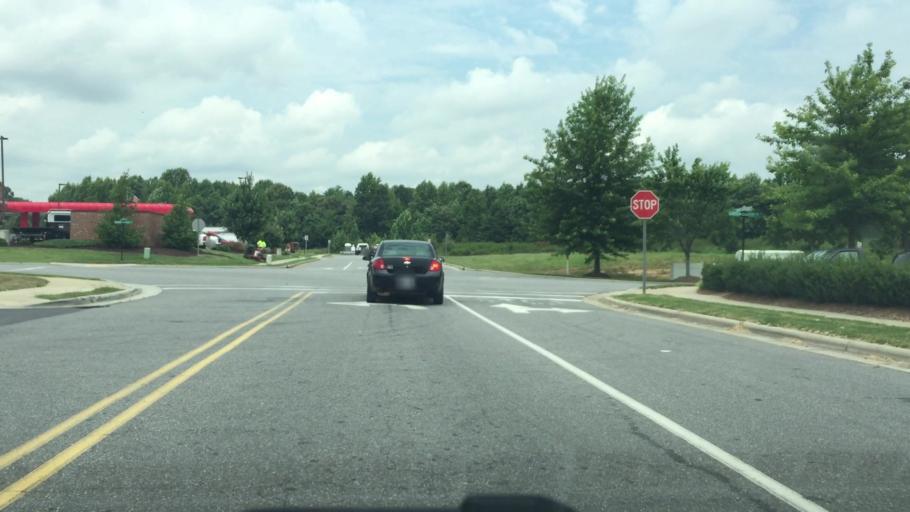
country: US
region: North Carolina
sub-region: Iredell County
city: Troutman
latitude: 35.6709
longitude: -80.8529
